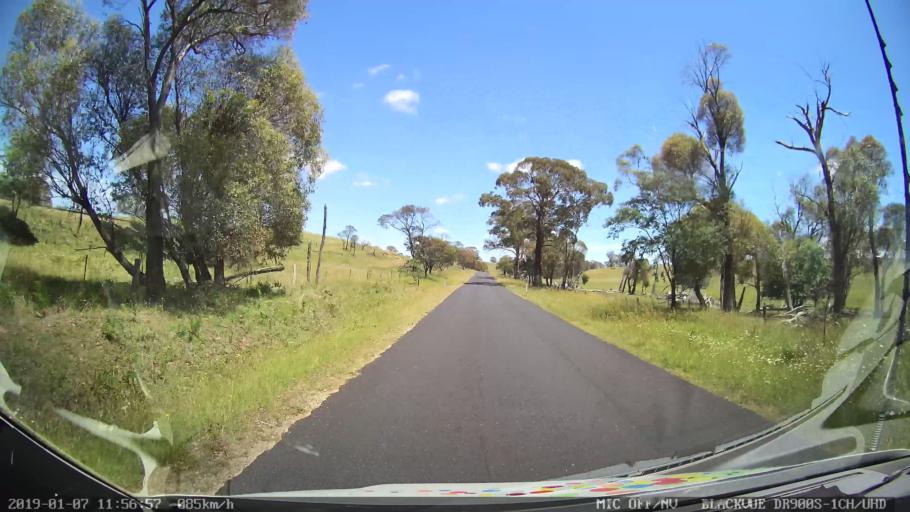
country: AU
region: New South Wales
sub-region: Guyra
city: Guyra
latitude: -30.2695
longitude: 151.6692
